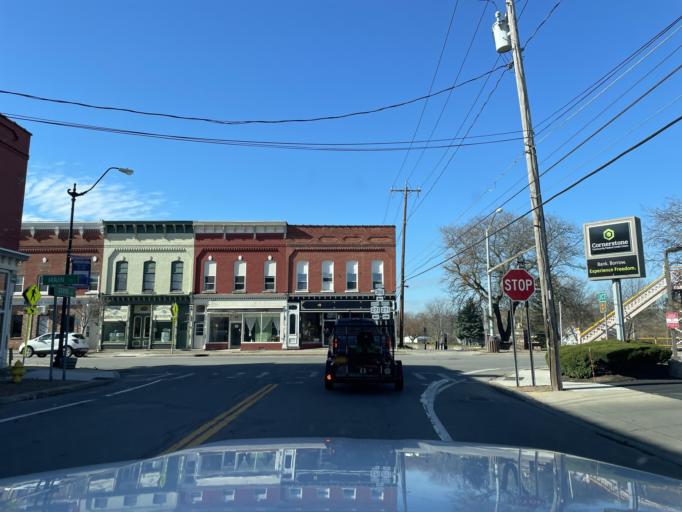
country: US
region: New York
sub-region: Niagara County
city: Middleport
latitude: 43.2125
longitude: -78.4760
